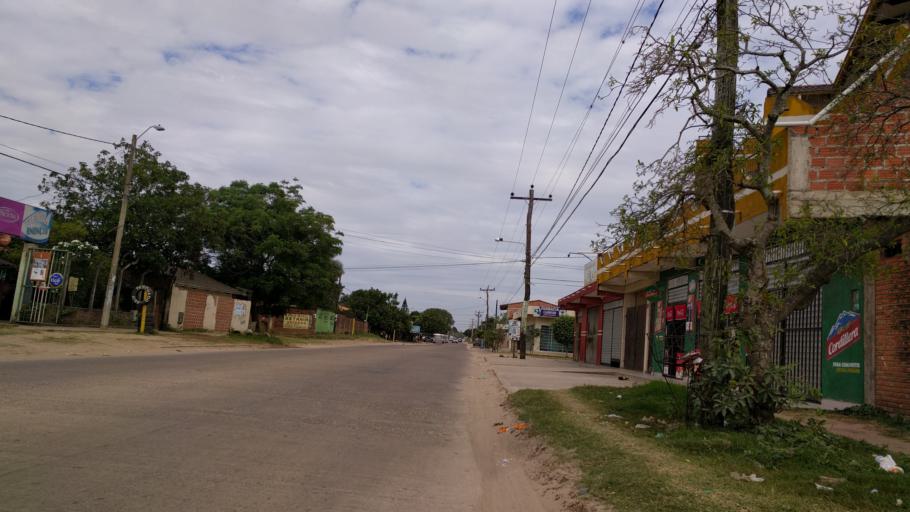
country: BO
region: Santa Cruz
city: Santa Cruz de la Sierra
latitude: -17.8167
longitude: -63.2321
